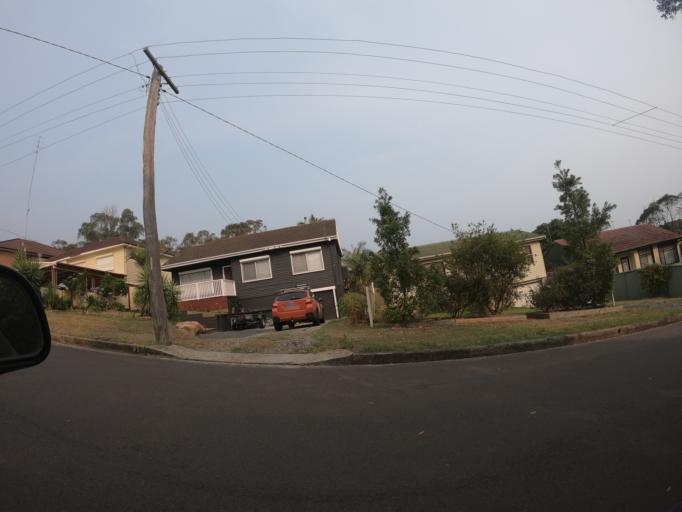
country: AU
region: New South Wales
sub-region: Wollongong
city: Cordeaux Heights
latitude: -34.4555
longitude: 150.8382
